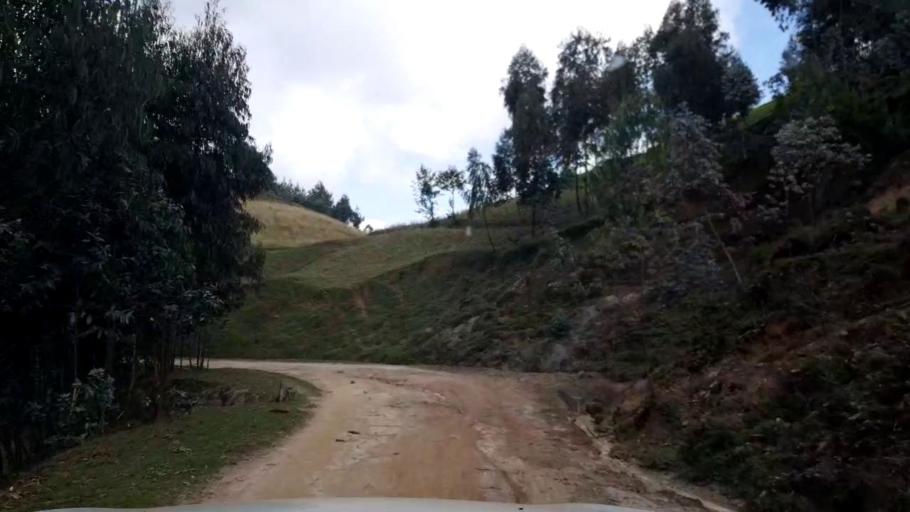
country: RW
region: Western Province
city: Kibuye
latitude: -1.8846
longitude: 29.4816
